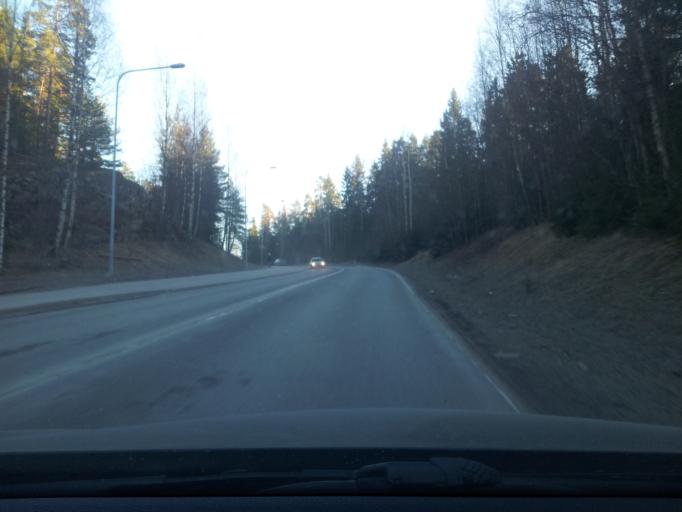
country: FI
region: Uusimaa
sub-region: Helsinki
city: Kauniainen
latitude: 60.1760
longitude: 24.7188
